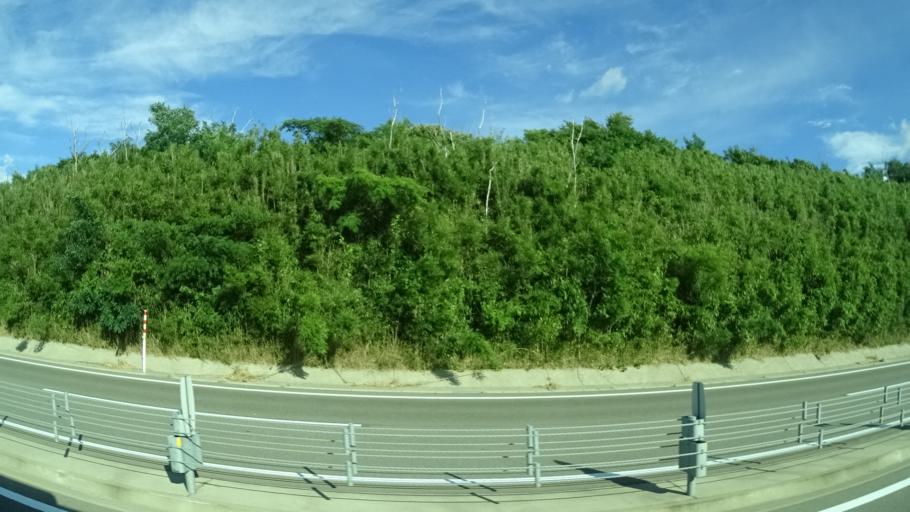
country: JP
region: Ishikawa
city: Tsubata
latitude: 36.6908
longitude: 136.6654
